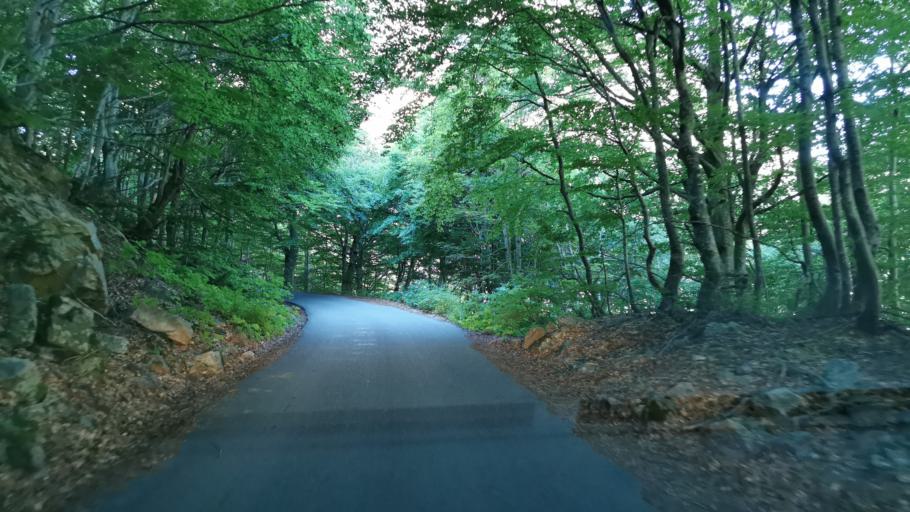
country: IT
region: Piedmont
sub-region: Provincia di Cuneo
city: Demonte
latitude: 44.2061
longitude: 7.2719
